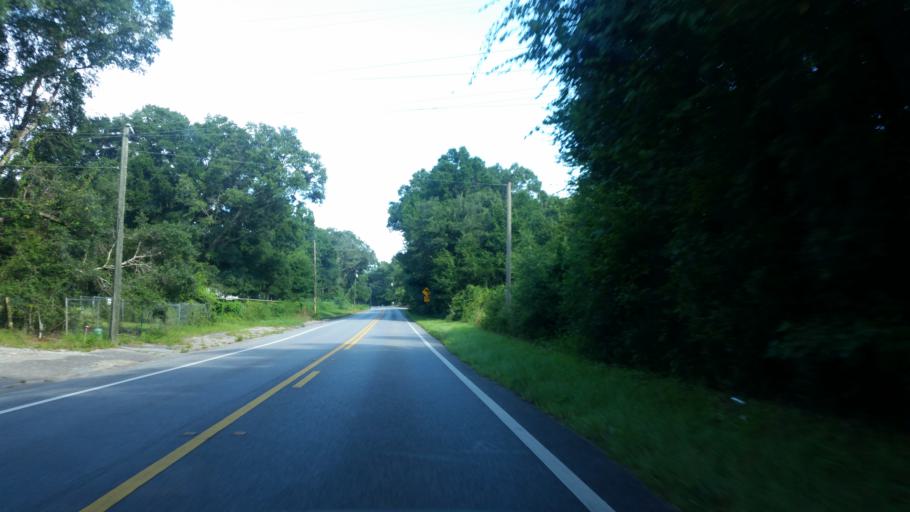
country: US
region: Florida
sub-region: Santa Rosa County
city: Milton
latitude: 30.6227
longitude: -87.0995
